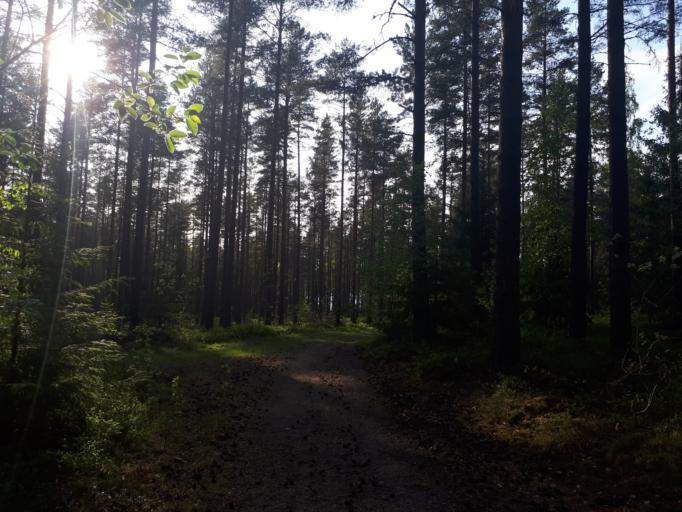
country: SE
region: Soedermanland
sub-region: Flens Kommun
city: Halleforsnas
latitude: 59.0651
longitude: 16.3988
